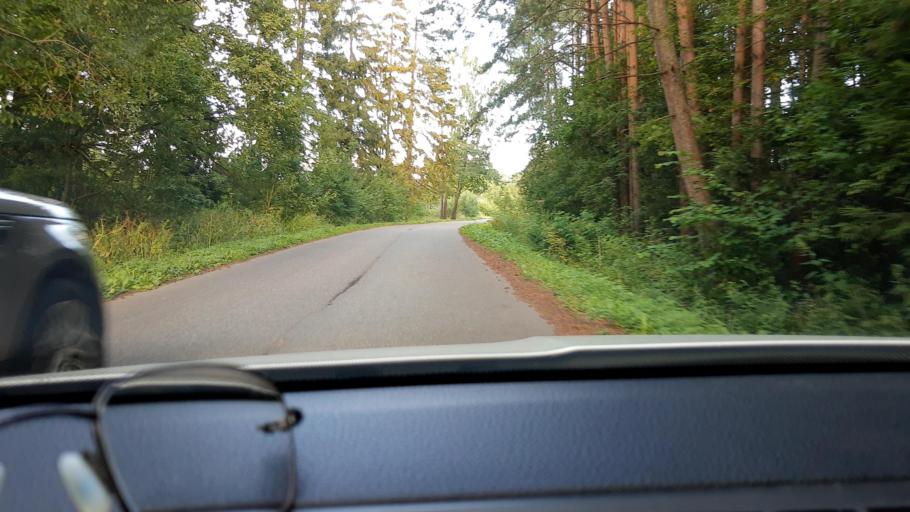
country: RU
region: Moskovskaya
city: Nazar'yevo
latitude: 55.6916
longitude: 37.0427
